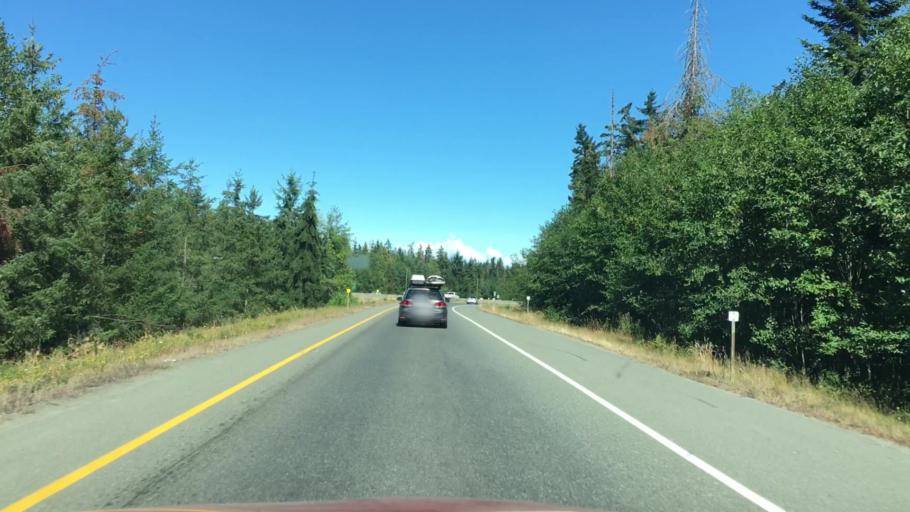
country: CA
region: British Columbia
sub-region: Regional District of Nanaimo
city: Parksville
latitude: 49.3242
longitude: -124.4378
